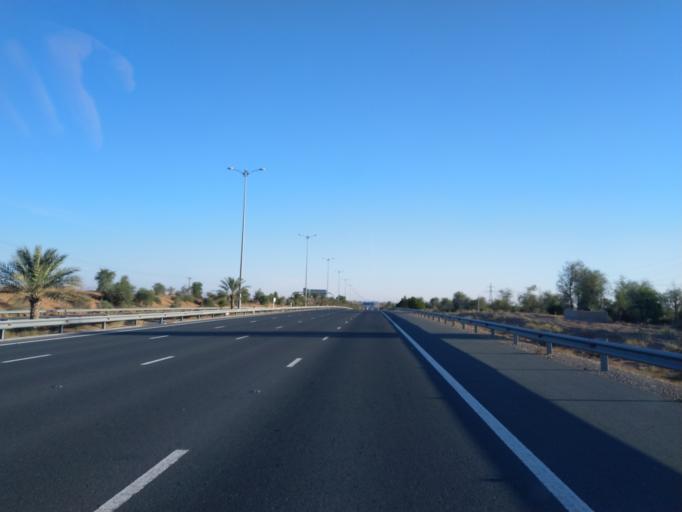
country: OM
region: Al Buraimi
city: Al Buraymi
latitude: 24.5381
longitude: 55.7576
